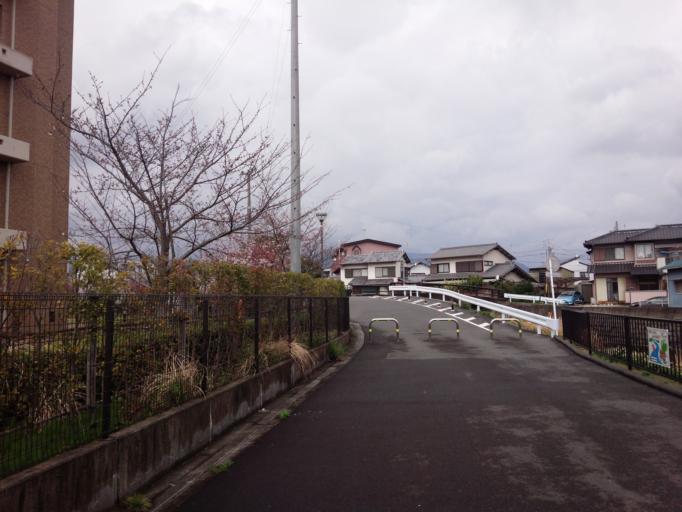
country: JP
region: Shizuoka
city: Shizuoka-shi
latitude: 35.0125
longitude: 138.4704
